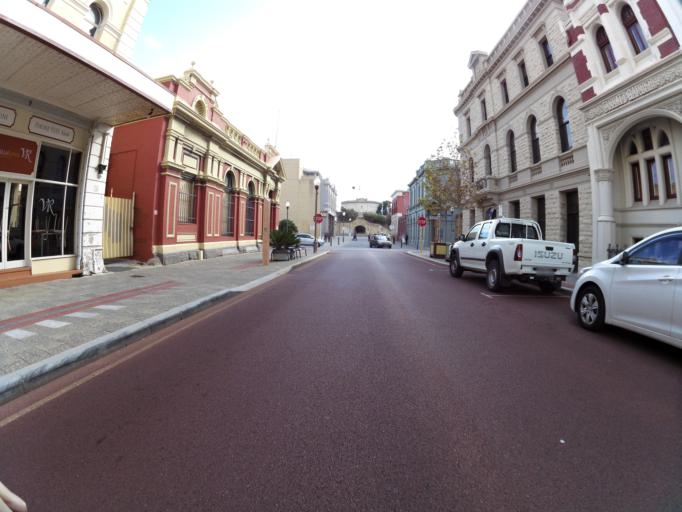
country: AU
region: Western Australia
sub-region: Fremantle
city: South Fremantle
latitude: -32.0557
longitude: 115.7423
